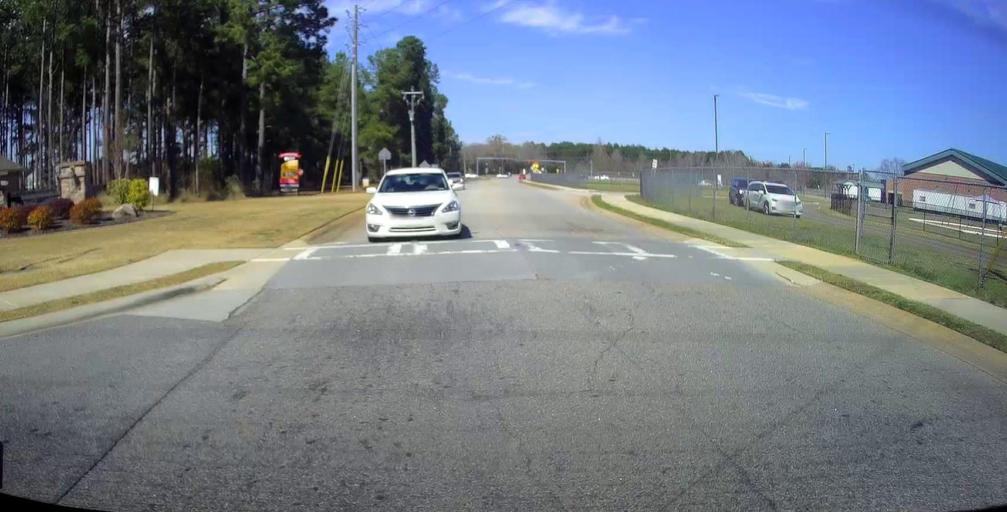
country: US
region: Georgia
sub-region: Houston County
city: Perry
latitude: 32.5041
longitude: -83.6524
